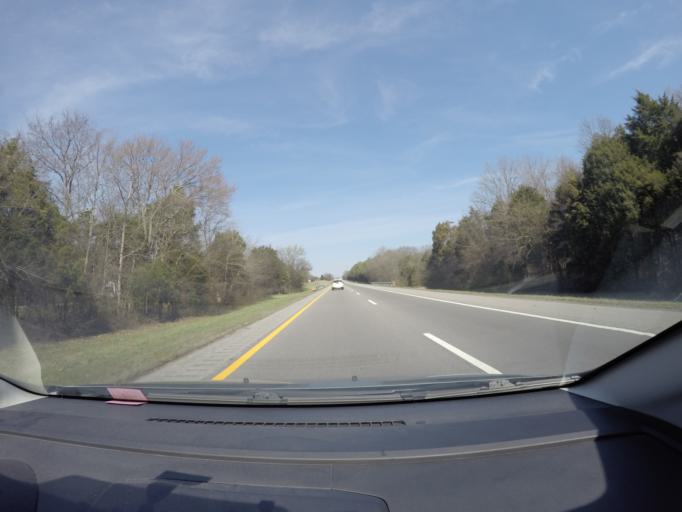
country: US
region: Tennessee
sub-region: Rutherford County
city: Plainview
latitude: 35.7391
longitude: -86.3338
